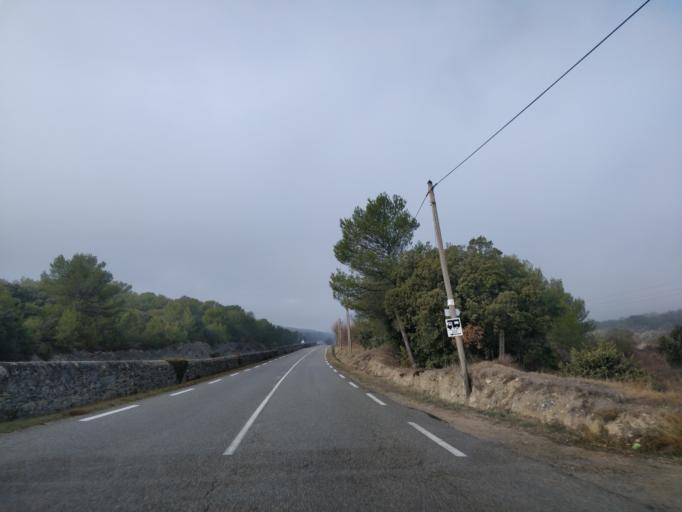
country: FR
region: Languedoc-Roussillon
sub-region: Departement du Gard
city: Caveirac
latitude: 43.8674
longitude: 4.3012
